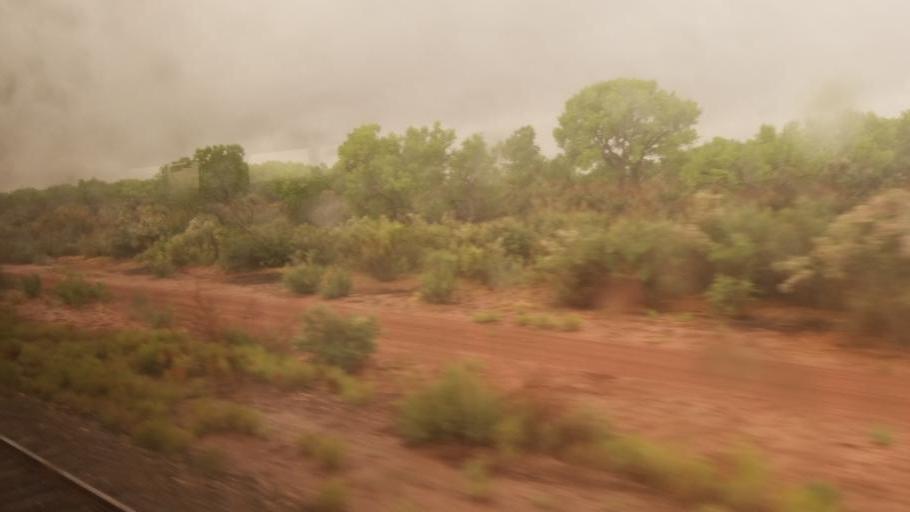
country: US
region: Arizona
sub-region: Navajo County
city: Holbrook
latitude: 34.9035
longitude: -110.2346
